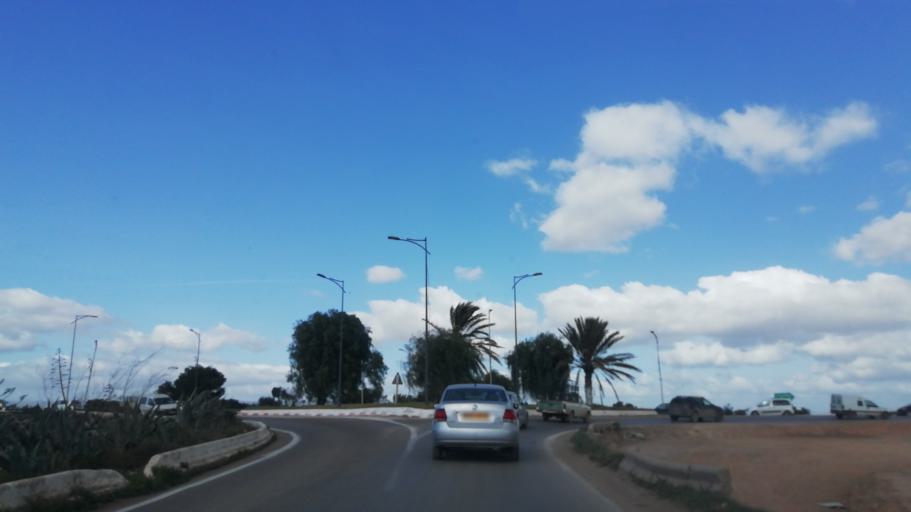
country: DZ
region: Oran
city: Es Senia
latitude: 35.6239
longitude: -0.5877
